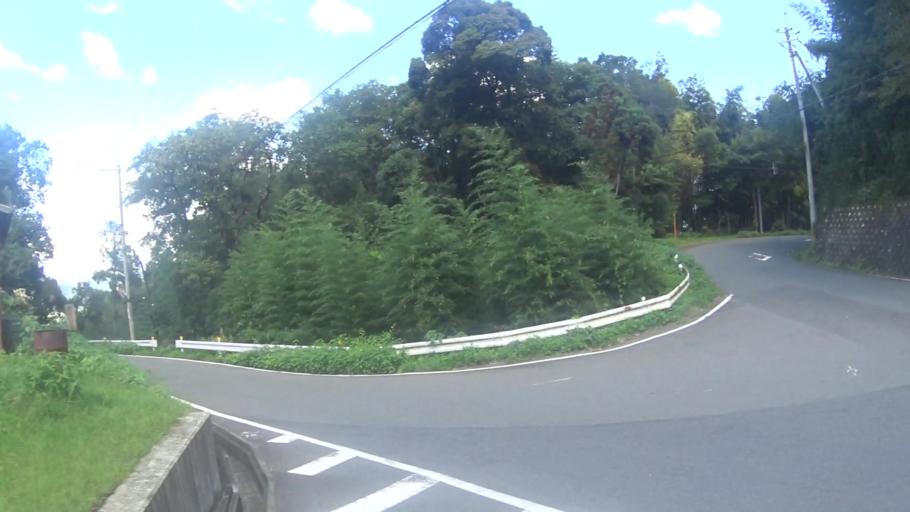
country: JP
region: Nara
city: Nara-shi
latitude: 34.7238
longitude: 135.8861
